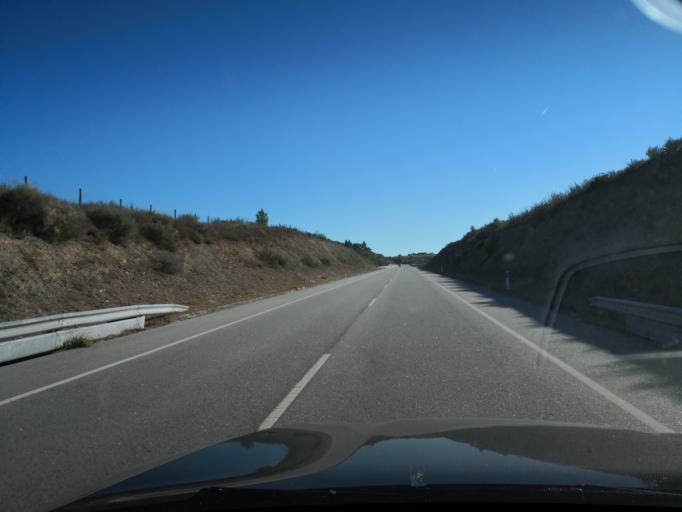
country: PT
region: Braganca
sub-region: Mirandela
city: Mirandela
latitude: 41.5081
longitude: -7.2288
